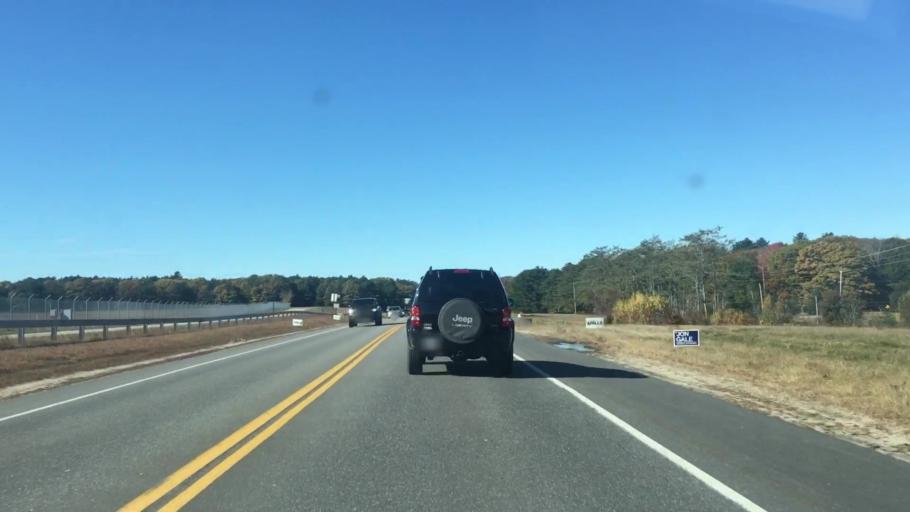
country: US
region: Maine
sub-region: Cumberland County
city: Brunswick
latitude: 43.9074
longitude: -69.9379
